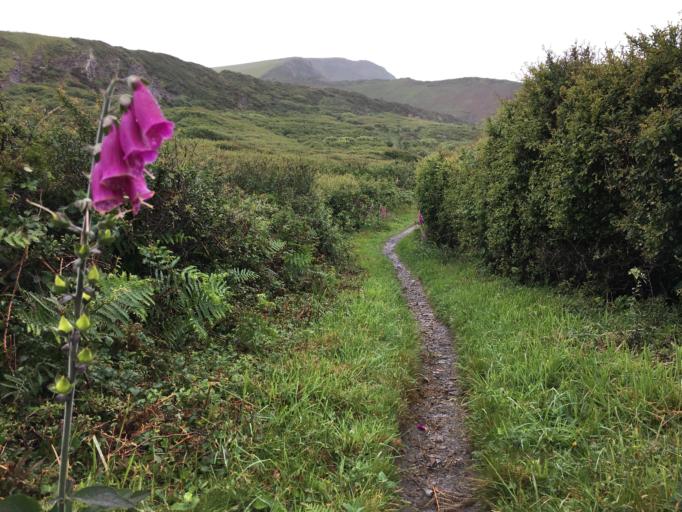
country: GB
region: England
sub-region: Cornwall
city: Jacobstow
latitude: 50.7256
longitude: -4.6469
